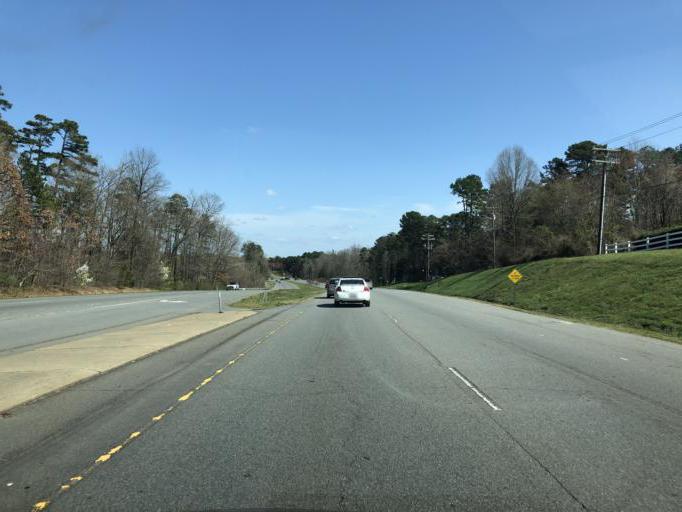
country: US
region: North Carolina
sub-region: Mecklenburg County
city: Huntersville
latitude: 35.3331
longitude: -80.8156
